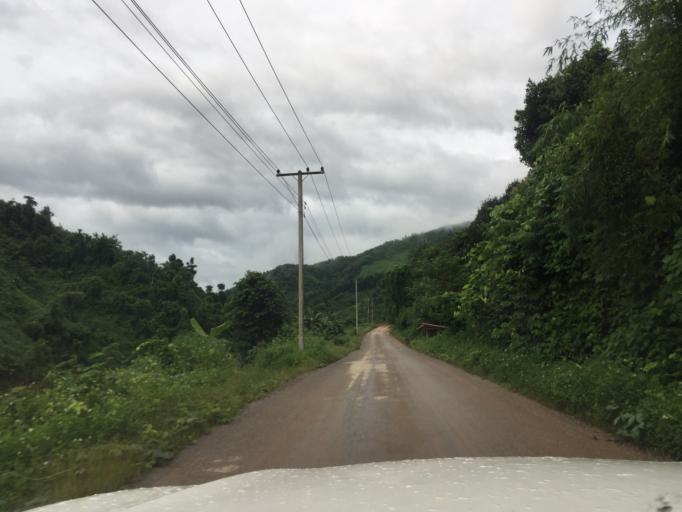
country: LA
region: Oudomxai
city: Muang La
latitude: 21.0245
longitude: 102.2341
